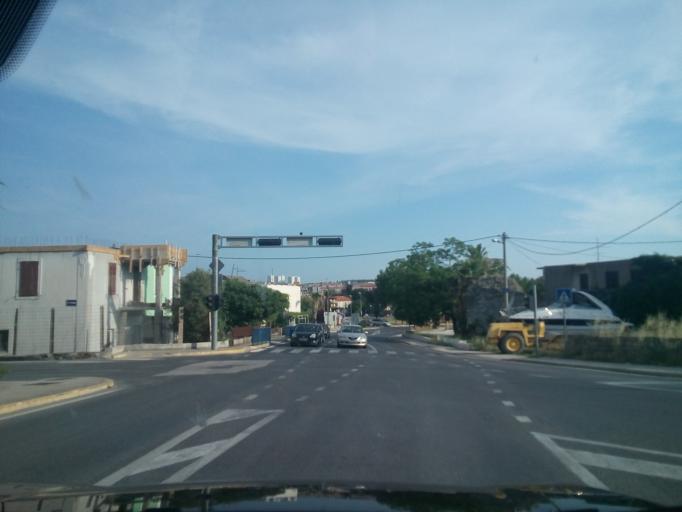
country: HR
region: Splitsko-Dalmatinska
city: Solin
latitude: 43.5421
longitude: 16.4918
